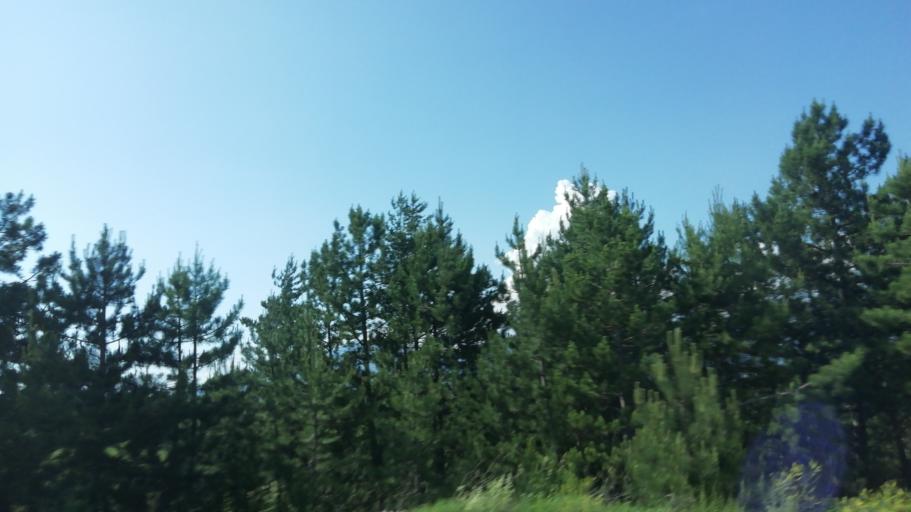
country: TR
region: Karabuk
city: Karabuk
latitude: 41.1266
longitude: 32.5998
